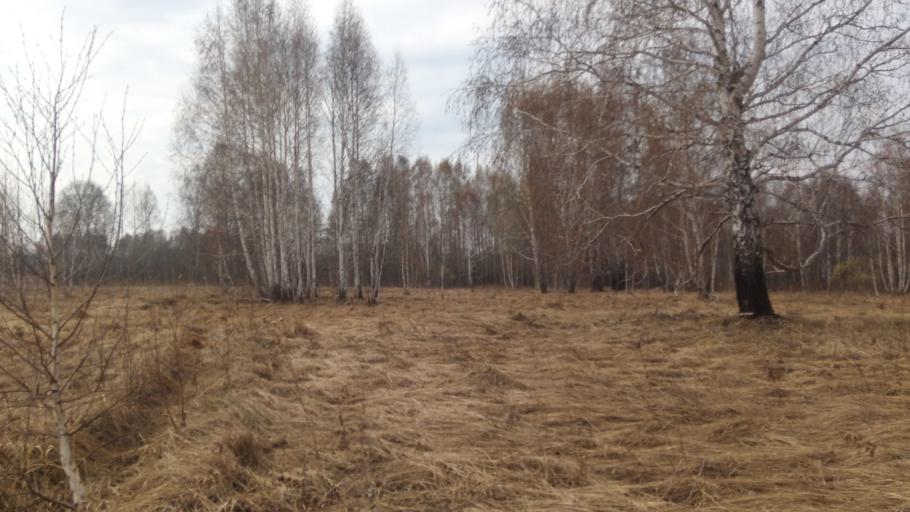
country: RU
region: Chelyabinsk
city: Timiryazevskiy
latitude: 54.9970
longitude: 60.8478
